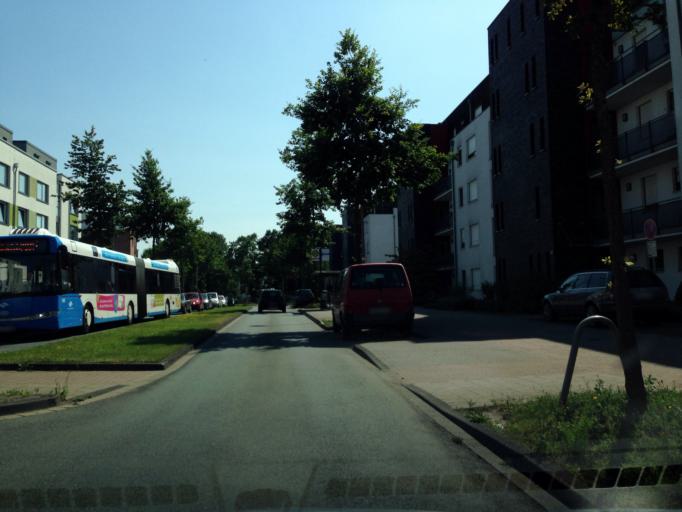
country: DE
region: North Rhine-Westphalia
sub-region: Regierungsbezirk Munster
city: Muenster
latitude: 51.9699
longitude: 7.5627
